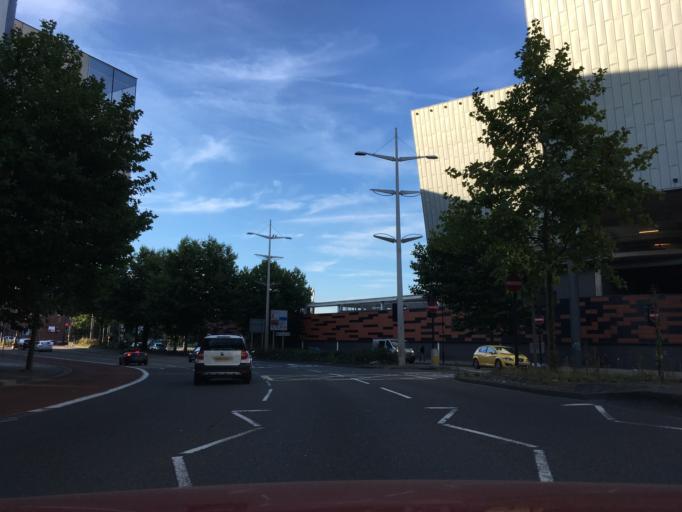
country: GB
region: England
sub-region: Bristol
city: Bristol
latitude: 51.4584
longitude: -2.5839
